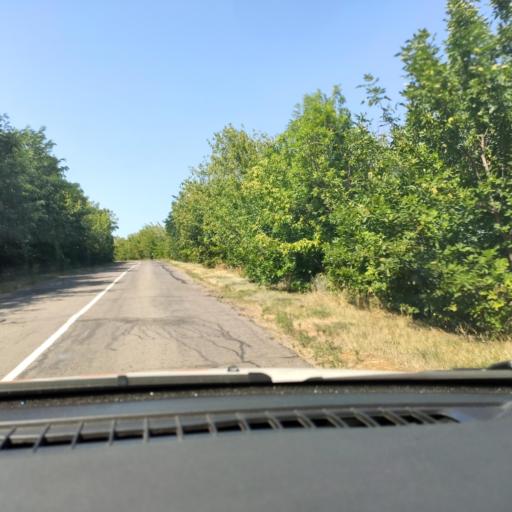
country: RU
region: Voronezj
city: Imeni Pervogo Maya
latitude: 50.7173
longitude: 39.3536
